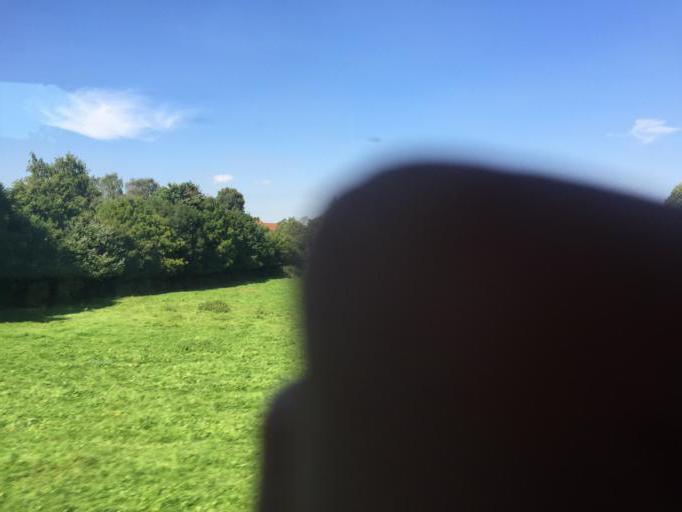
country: DE
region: Schleswig-Holstein
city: Ratekau
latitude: 53.9468
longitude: 10.7399
